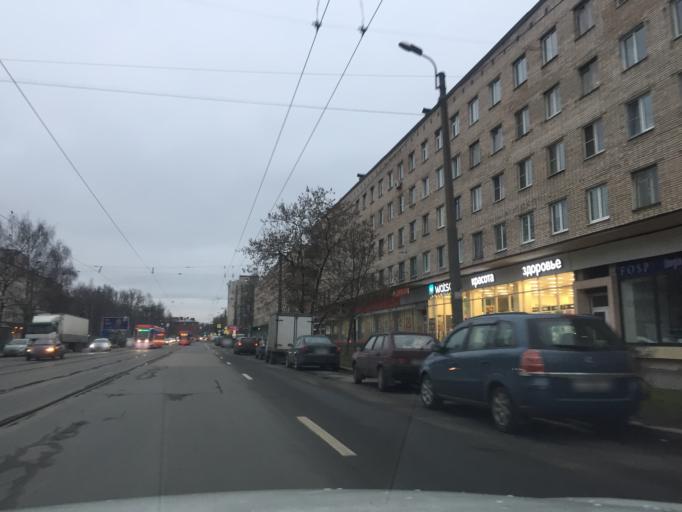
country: RU
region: St.-Petersburg
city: Sosnovka
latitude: 60.0147
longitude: 30.3680
